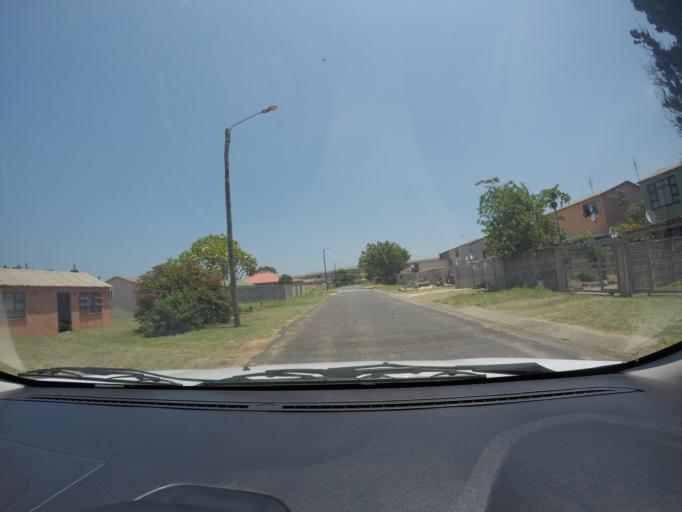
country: ZA
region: KwaZulu-Natal
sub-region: uThungulu District Municipality
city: eSikhawini
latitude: -28.8828
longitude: 31.8928
